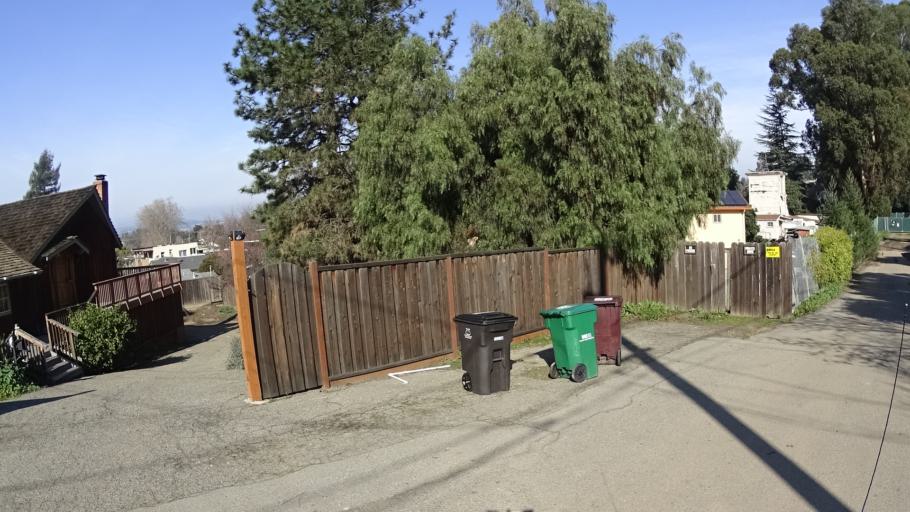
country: US
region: California
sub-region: Alameda County
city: Fairview
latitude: 37.6814
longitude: -122.0629
